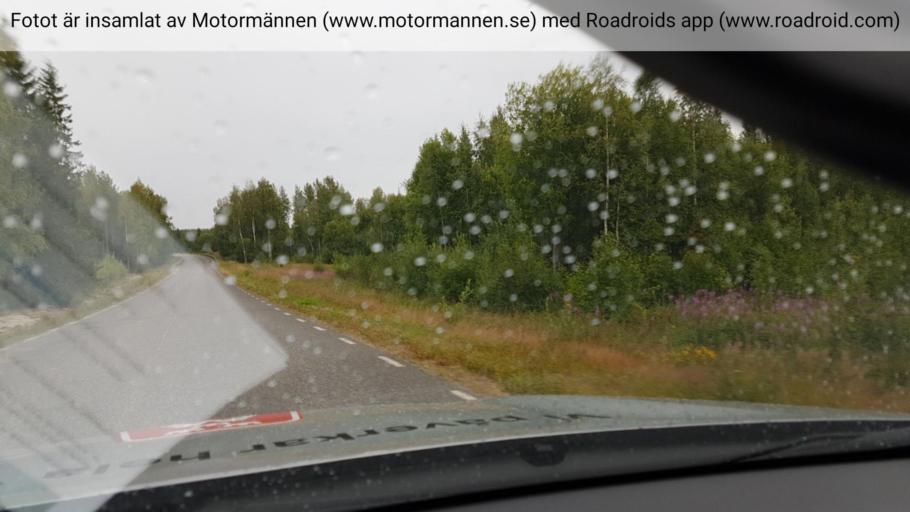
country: SE
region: Norrbotten
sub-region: Bodens Kommun
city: Boden
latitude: 65.8718
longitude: 21.3808
